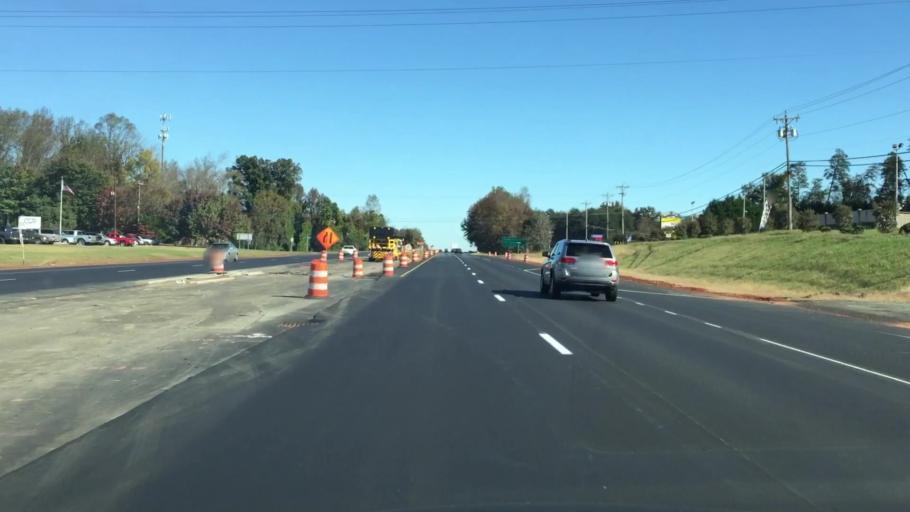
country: US
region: North Carolina
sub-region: Guilford County
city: McLeansville
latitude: 36.1608
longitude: -79.7224
